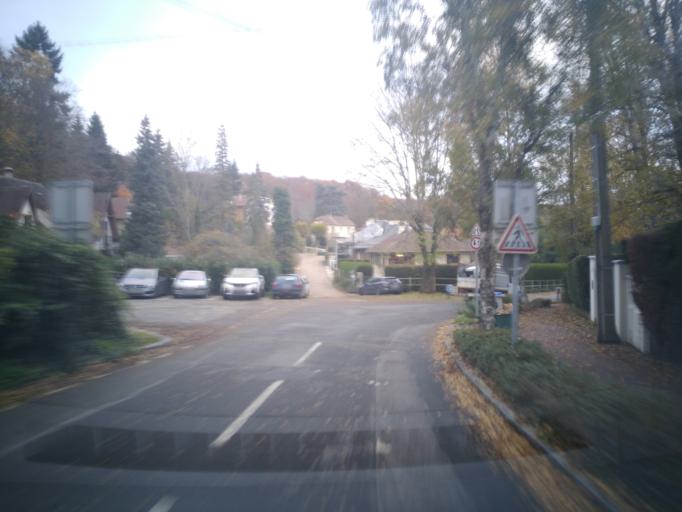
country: FR
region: Ile-de-France
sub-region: Departement des Yvelines
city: Fourqueux
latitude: 48.8690
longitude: 2.0528
